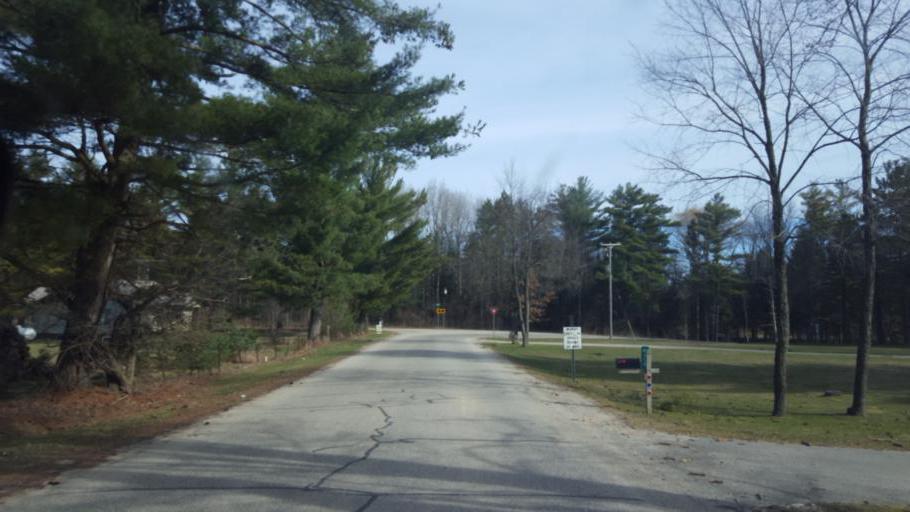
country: US
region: Michigan
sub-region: Mecosta County
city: Big Rapids
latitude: 43.5612
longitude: -85.5228
